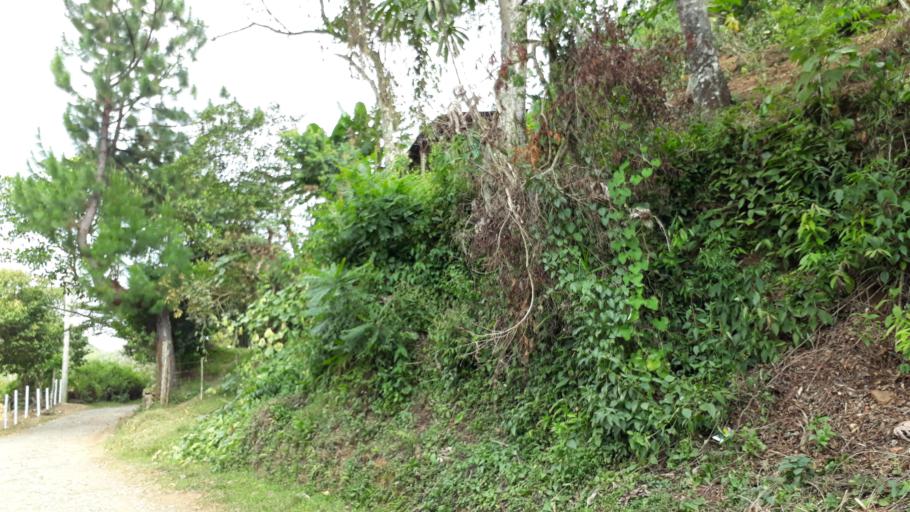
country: CO
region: Valle del Cauca
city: Jamundi
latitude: 3.2222
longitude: -76.6263
